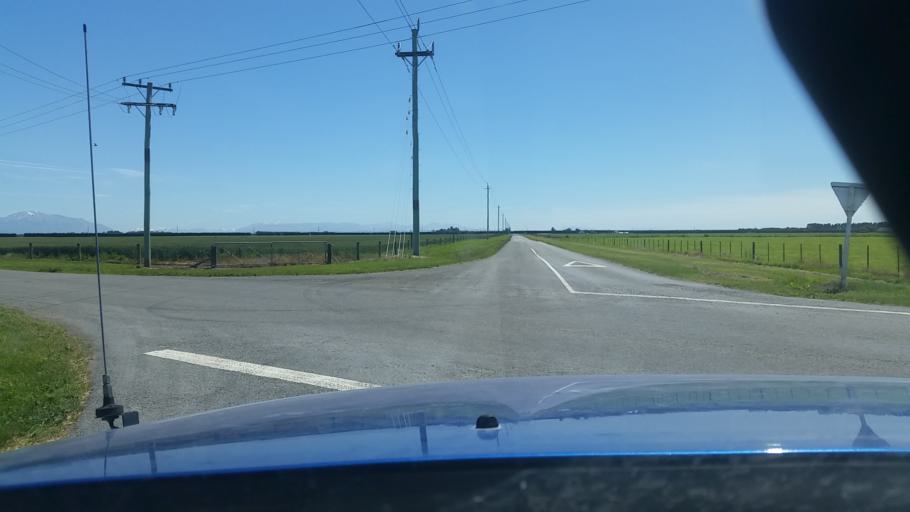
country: NZ
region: Canterbury
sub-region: Ashburton District
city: Ashburton
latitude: -43.8924
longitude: 171.8526
